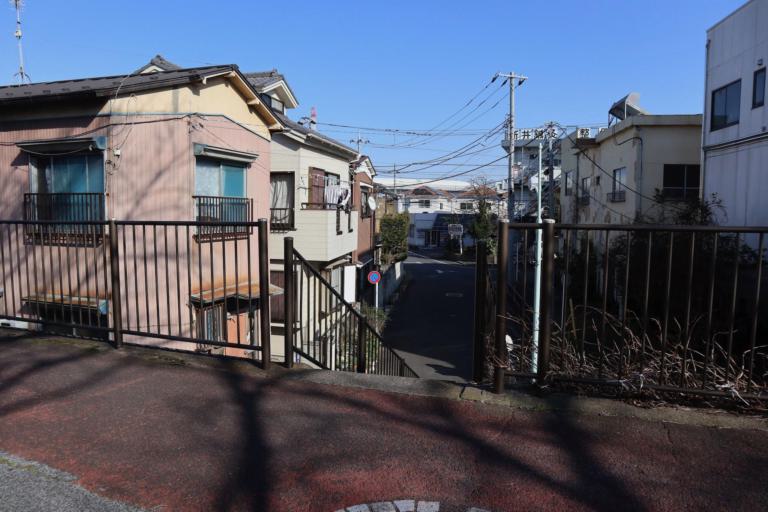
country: JP
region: Chiba
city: Matsudo
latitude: 35.7776
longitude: 139.8830
